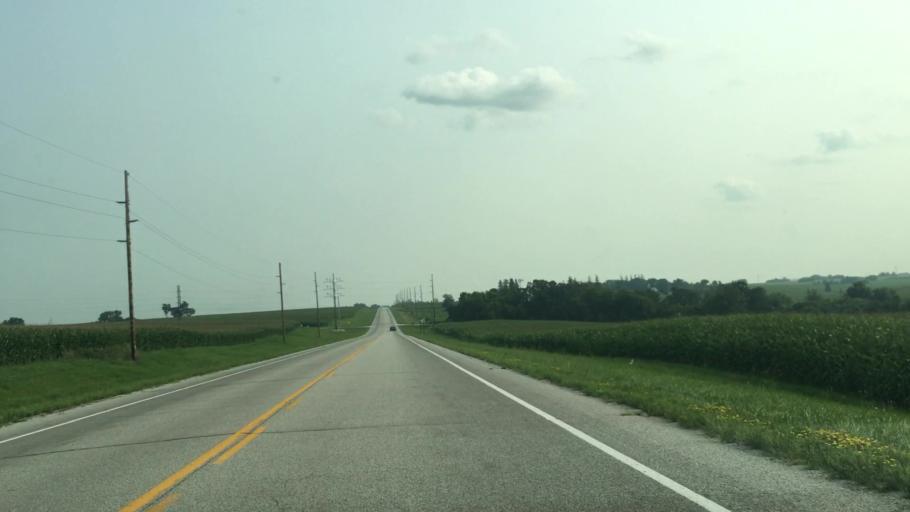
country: US
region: Minnesota
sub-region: Fillmore County
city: Harmony
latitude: 43.5689
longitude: -91.9299
